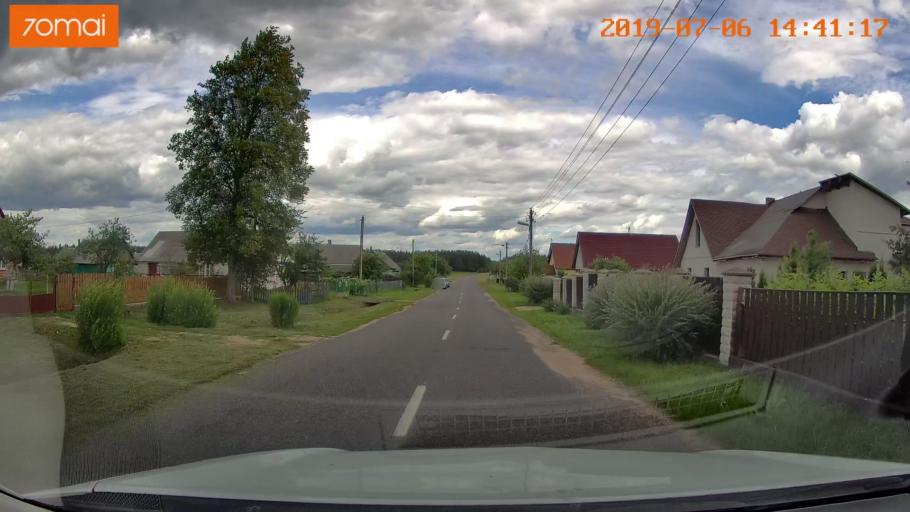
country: BY
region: Minsk
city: Ivyanyets
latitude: 53.9309
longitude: 26.6763
